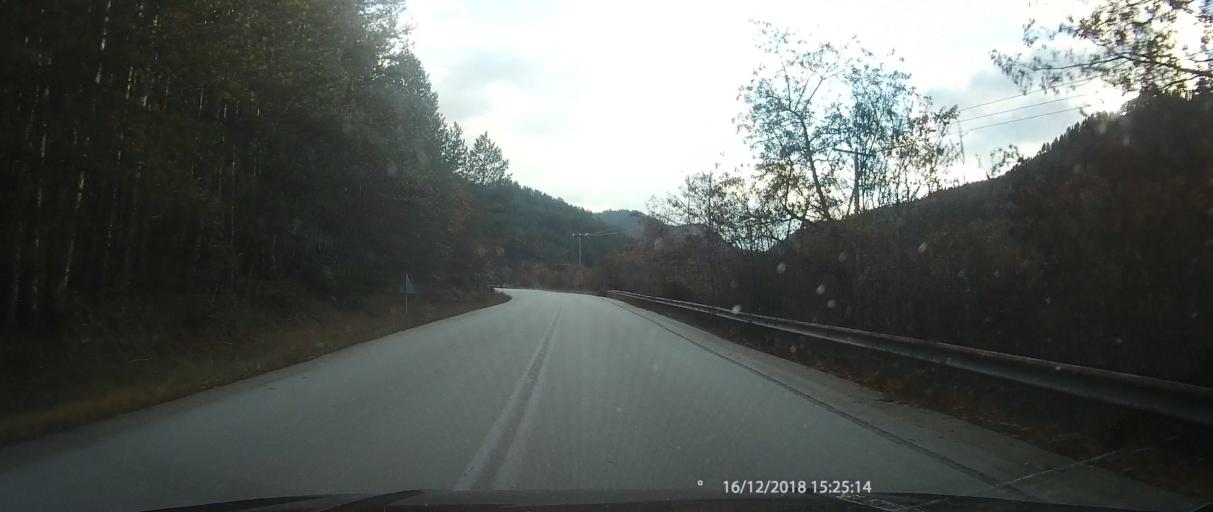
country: GR
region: Epirus
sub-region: Nomos Ioanninon
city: Konitsa
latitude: 40.1307
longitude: 20.7819
